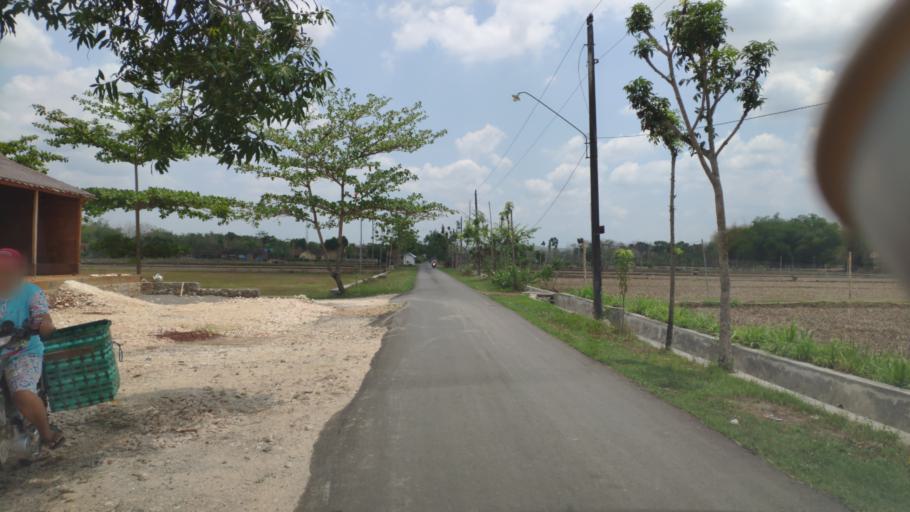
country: ID
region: Central Java
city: Mojo Wetan
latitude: -7.0321
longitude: 111.3727
